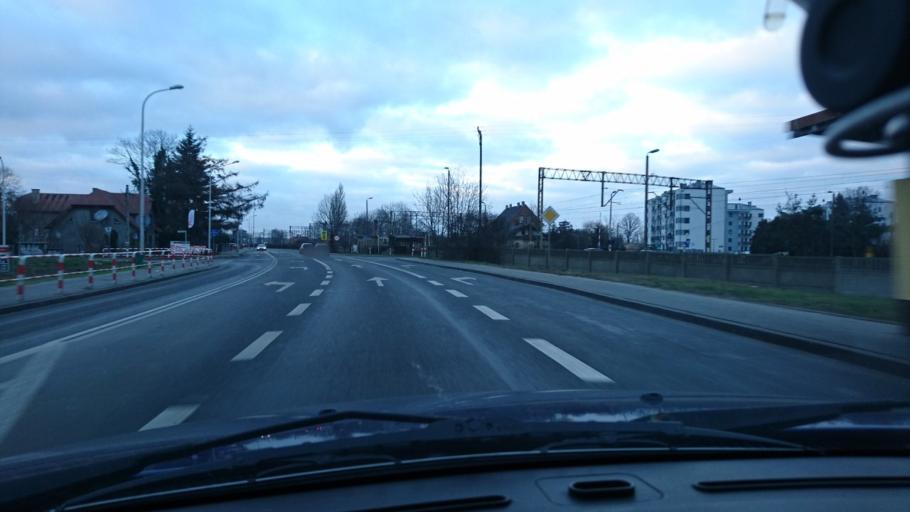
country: PL
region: Greater Poland Voivodeship
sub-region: Powiat kepinski
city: Kepno
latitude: 51.2974
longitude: 17.9973
